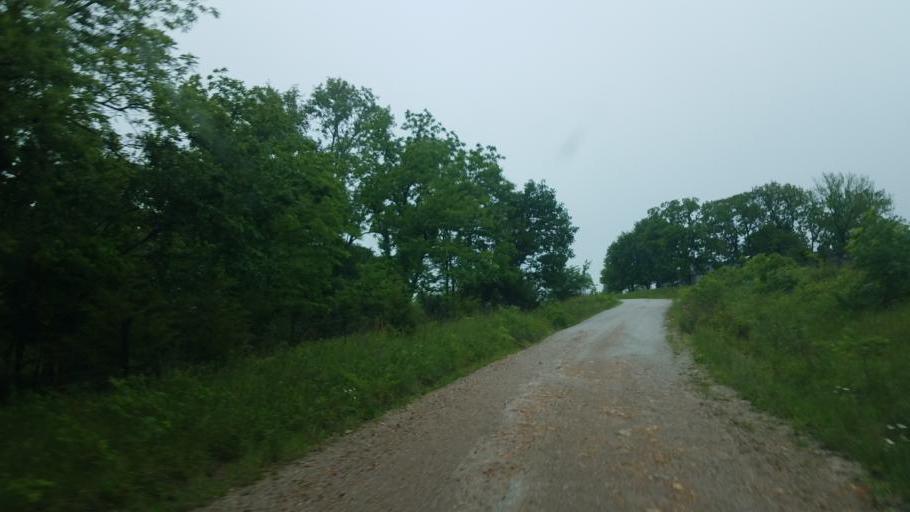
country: US
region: Missouri
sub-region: Moniteau County
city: California
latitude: 38.7585
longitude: -92.6068
